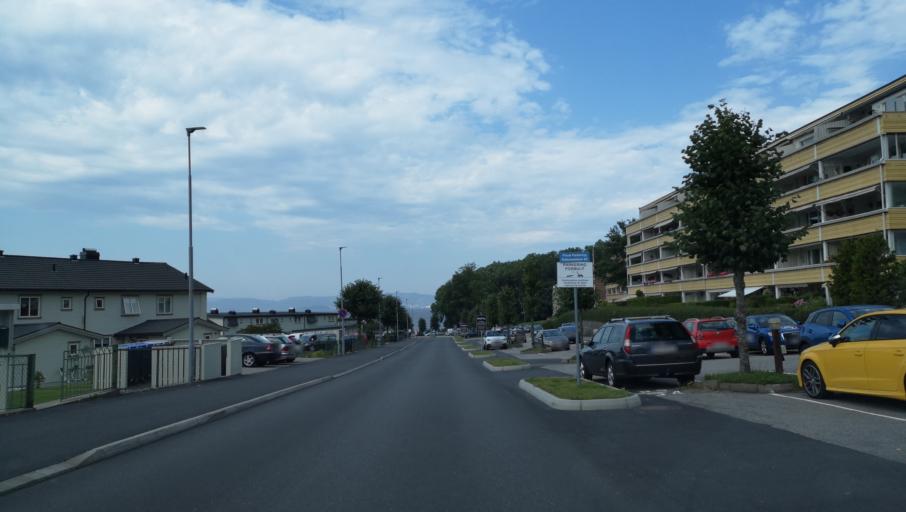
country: NO
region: Ostfold
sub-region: Moss
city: Moss
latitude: 59.4456
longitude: 10.6176
